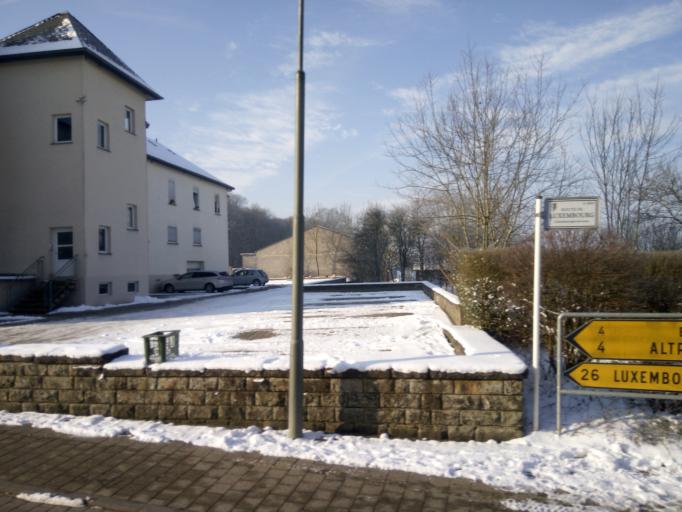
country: LU
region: Grevenmacher
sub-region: Canton d'Echternach
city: Consdorf
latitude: 49.7734
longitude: 6.3412
